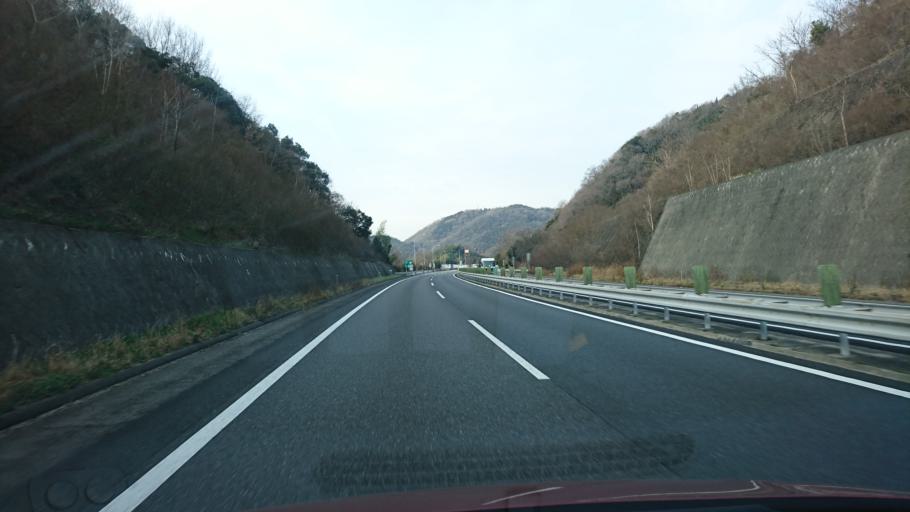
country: JP
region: Okayama
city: Okayama-shi
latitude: 34.7693
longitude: 134.0789
